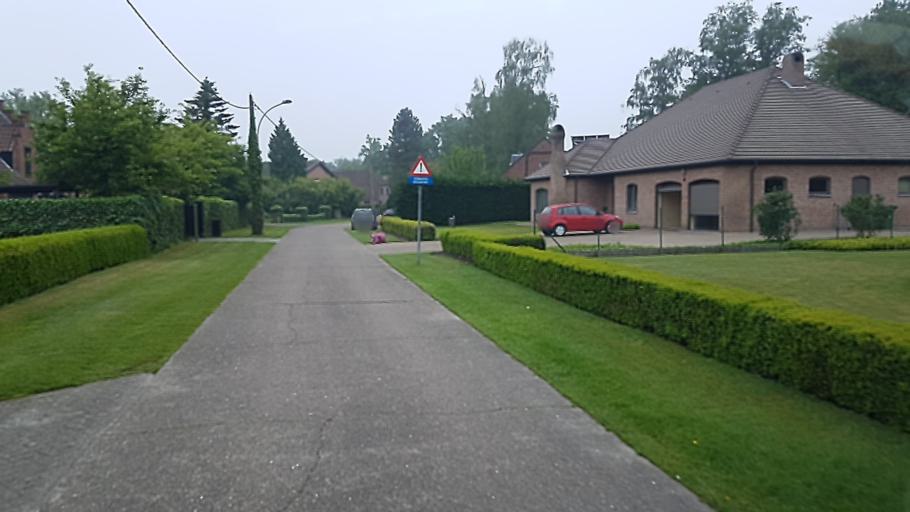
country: BE
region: Flanders
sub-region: Provincie Antwerpen
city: Zandhoven
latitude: 51.2739
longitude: 4.6521
